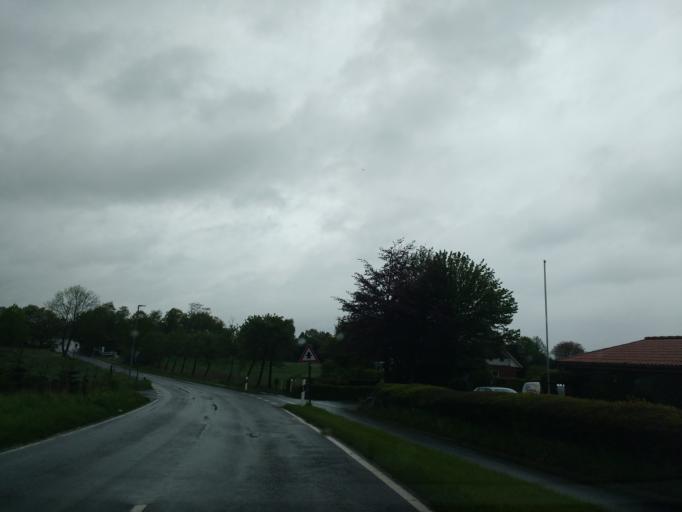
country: DE
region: Schleswig-Holstein
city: Waabs
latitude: 54.5502
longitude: 9.9927
